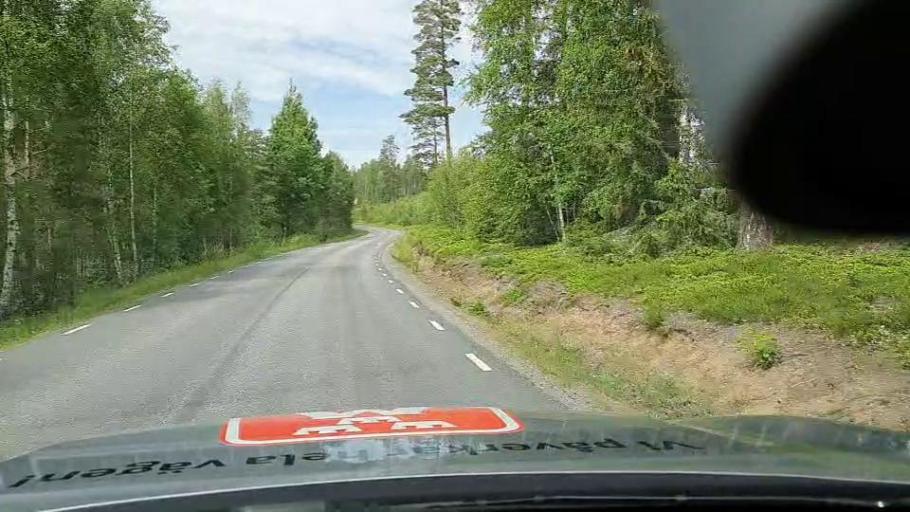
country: SE
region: Soedermanland
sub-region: Eskilstuna Kommun
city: Arla
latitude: 59.2447
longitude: 16.7181
